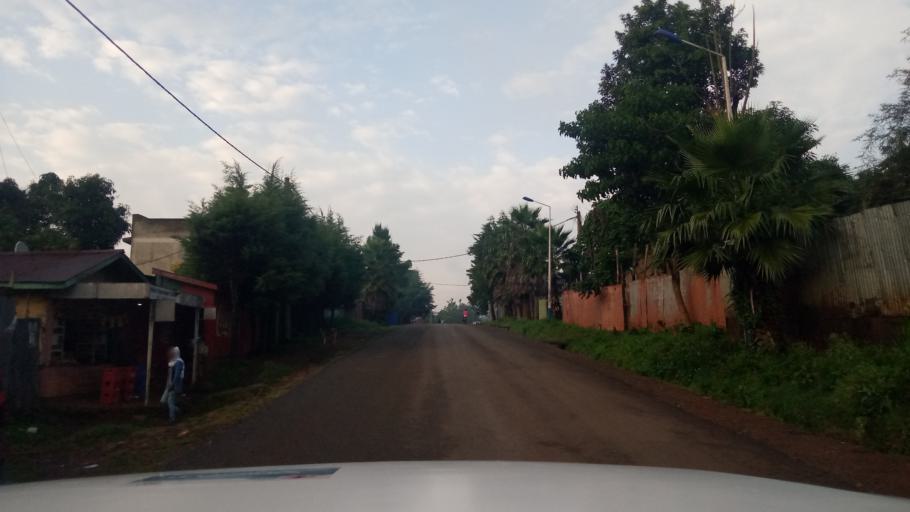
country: ET
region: Oromiya
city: Jima
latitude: 7.6789
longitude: 36.8400
